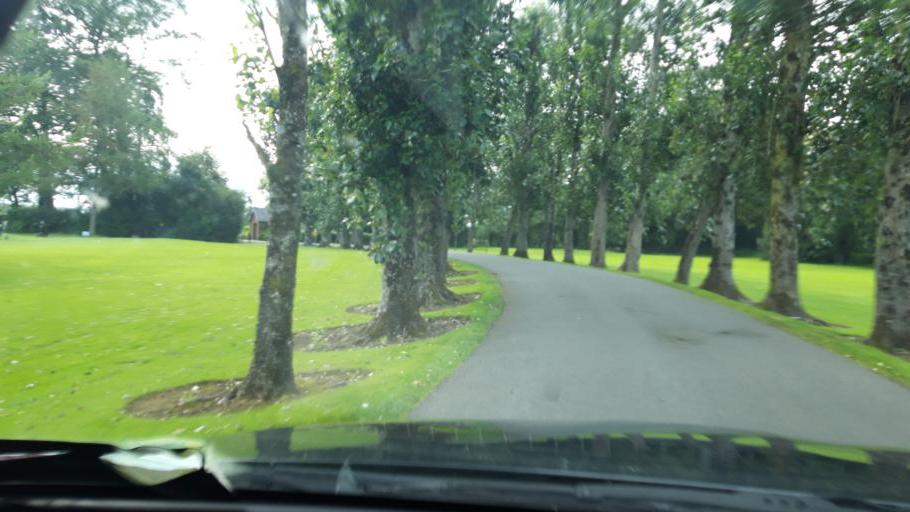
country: IE
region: Leinster
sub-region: Lu
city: Dundalk
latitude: 54.0331
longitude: -6.3580
